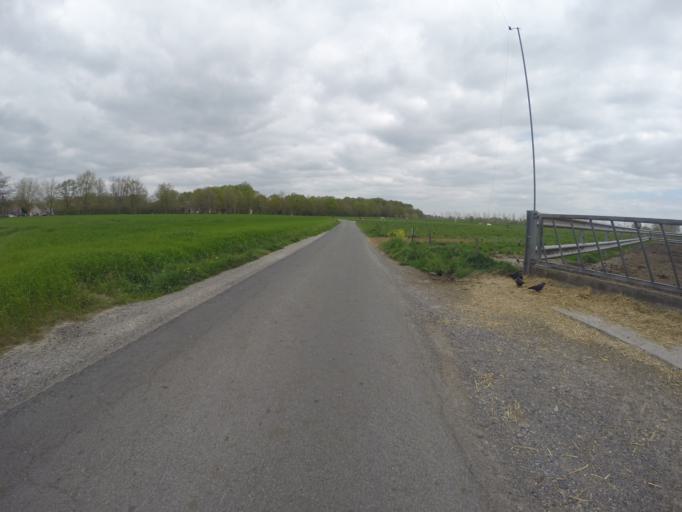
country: BE
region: Flanders
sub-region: Provincie Oost-Vlaanderen
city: Aalter
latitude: 51.0380
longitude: 3.4480
